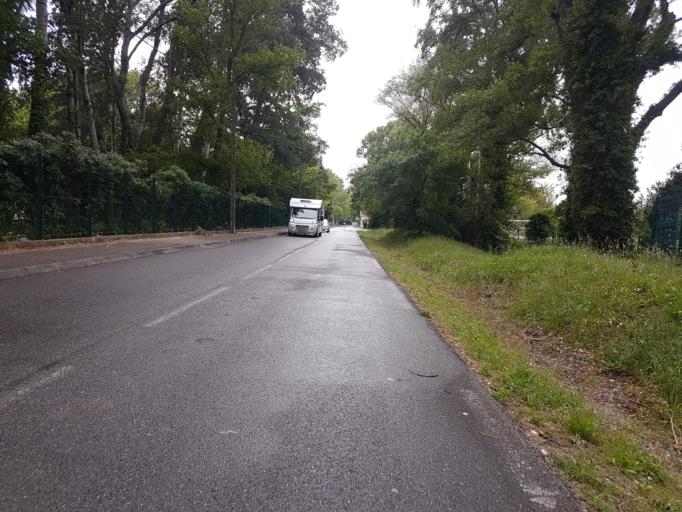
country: FR
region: Provence-Alpes-Cote d'Azur
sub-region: Departement du Vaucluse
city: Avignon
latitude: 43.9561
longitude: 4.8004
